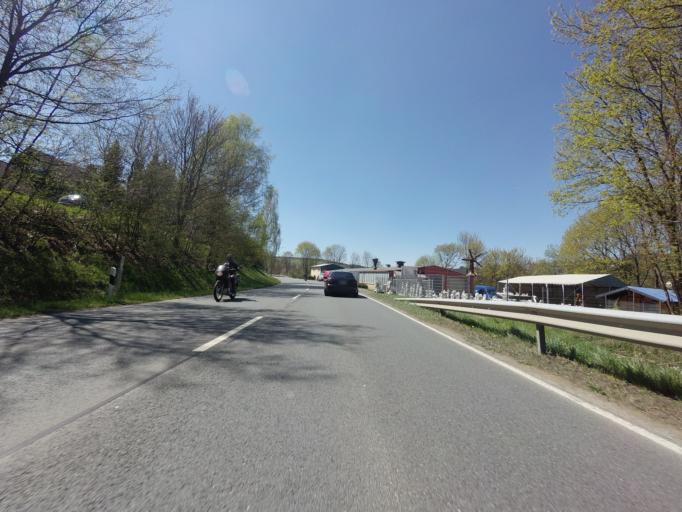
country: DE
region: North Rhine-Westphalia
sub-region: Regierungsbezirk Arnsberg
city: Erndtebruck
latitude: 50.9940
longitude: 8.2616
